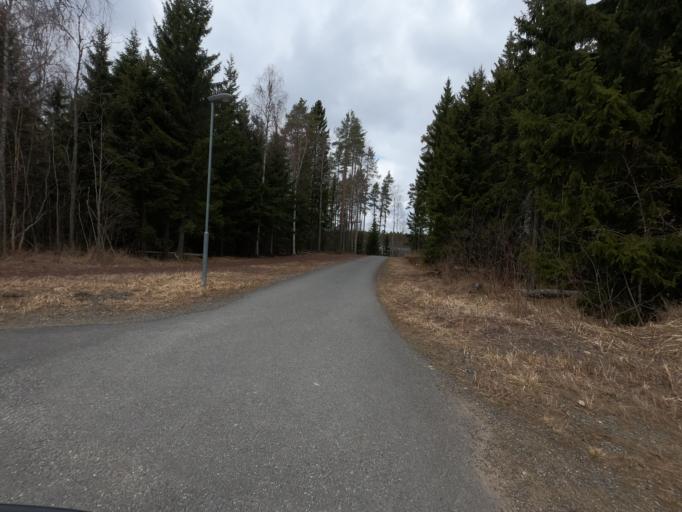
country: FI
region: North Karelia
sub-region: Joensuu
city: Joensuu
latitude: 62.5693
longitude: 29.8136
